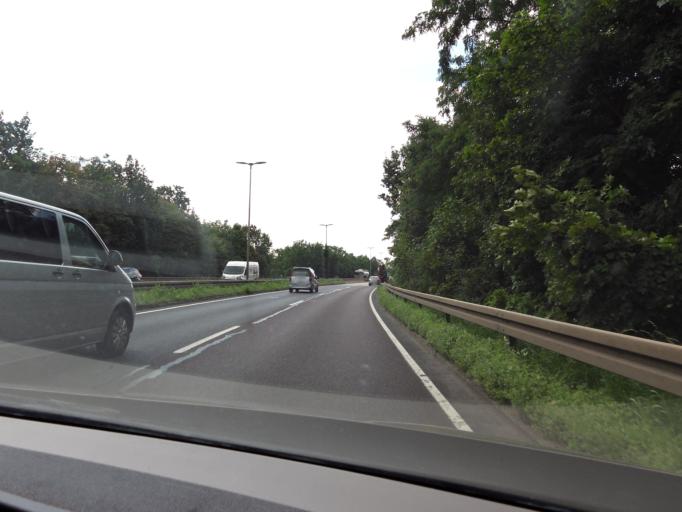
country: DE
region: Saxony-Anhalt
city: Magdeburg
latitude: 52.1240
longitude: 11.6183
